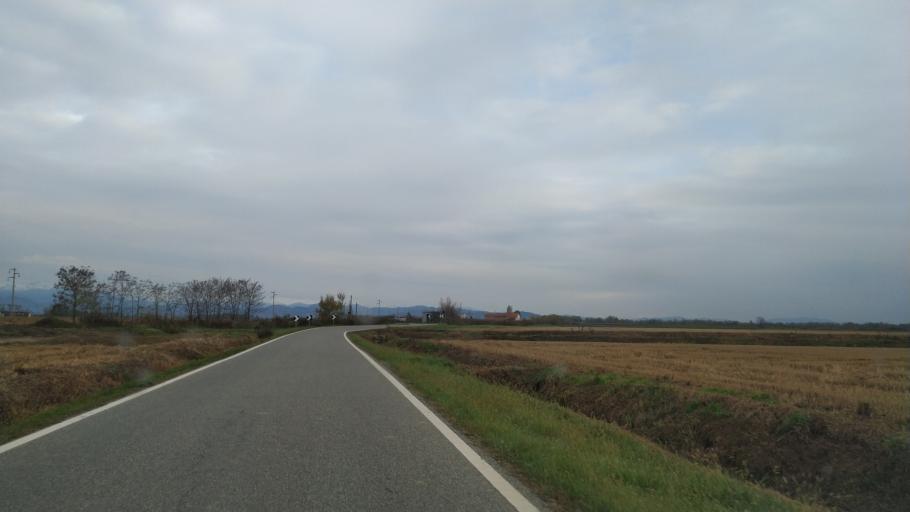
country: IT
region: Piedmont
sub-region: Provincia di Vercelli
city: Buronzo
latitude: 45.4887
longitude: 8.2804
